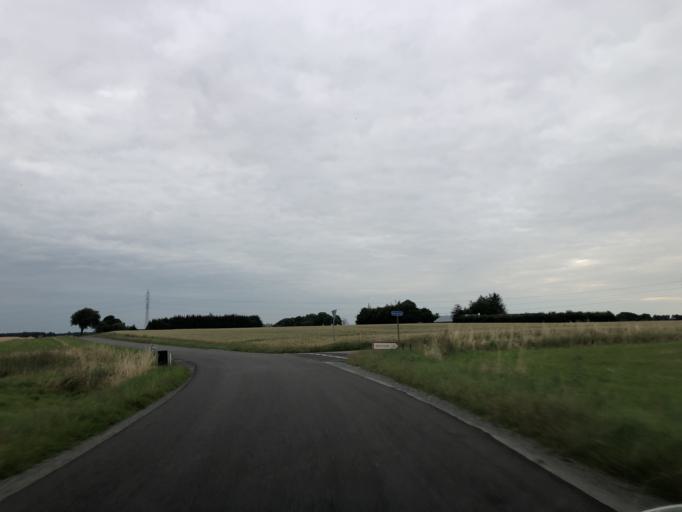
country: DK
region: South Denmark
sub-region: Vejle Kommune
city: Jelling
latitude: 55.7215
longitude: 9.3957
